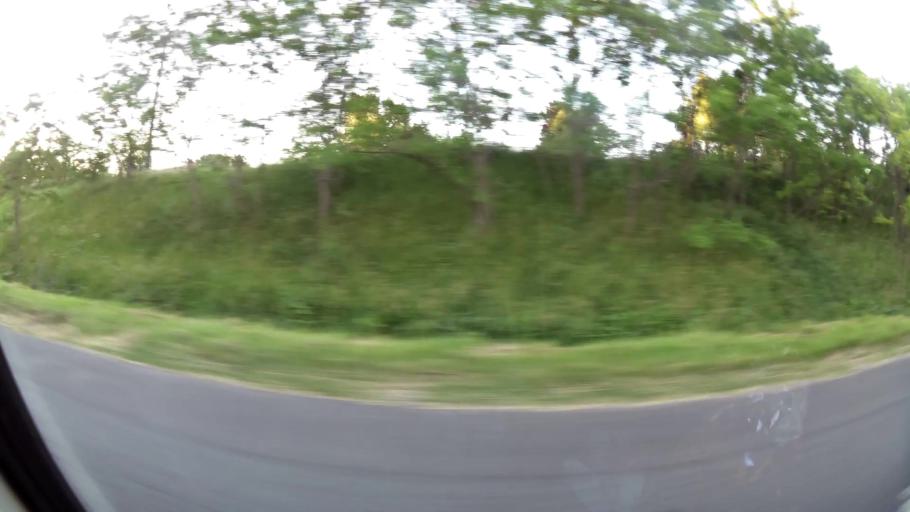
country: AR
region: Buenos Aires
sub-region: Partido de Quilmes
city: Quilmes
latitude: -34.8185
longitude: -58.1856
